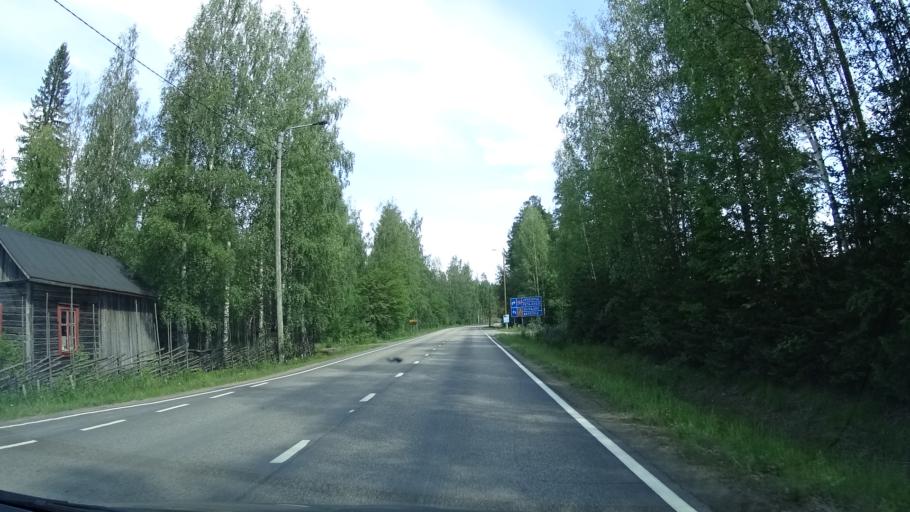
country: FI
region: Central Finland
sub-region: Keuruu
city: Multia
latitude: 62.4146
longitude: 24.8194
